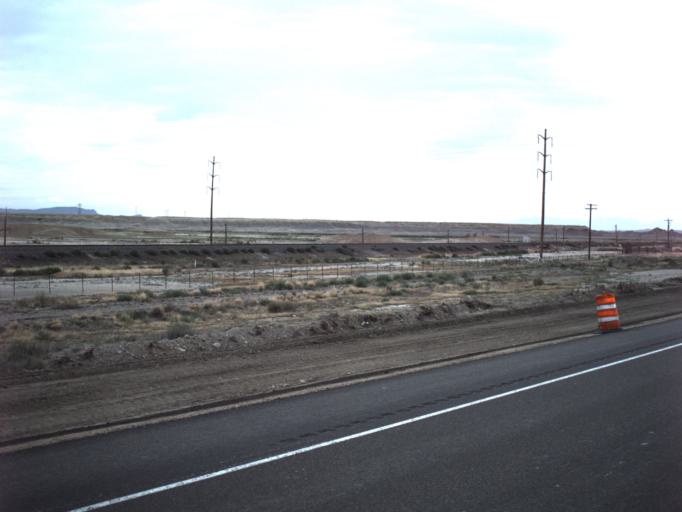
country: US
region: Utah
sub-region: Carbon County
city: East Carbon City
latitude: 39.0268
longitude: -110.3007
